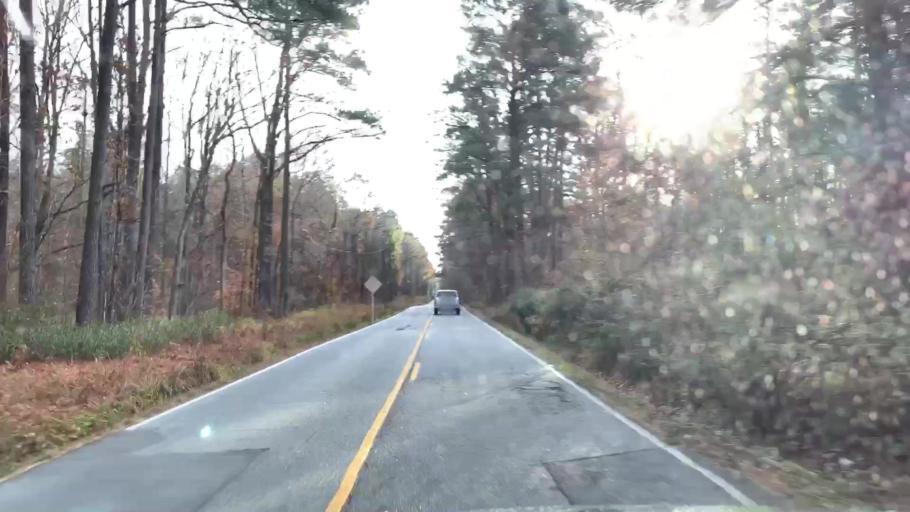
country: US
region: Virginia
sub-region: City of Virginia Beach
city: Virginia Beach
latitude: 36.7409
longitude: -76.1118
